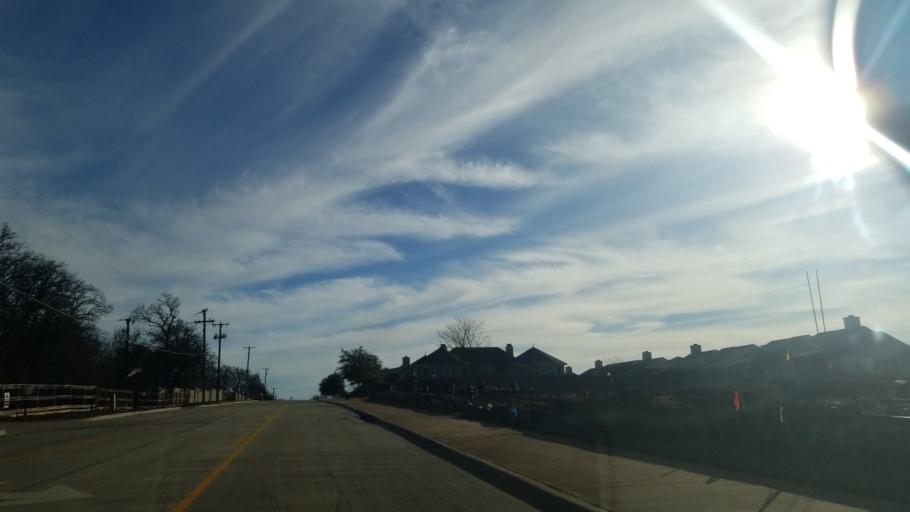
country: US
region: Texas
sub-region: Denton County
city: Corinth
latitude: 33.1436
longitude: -97.0559
